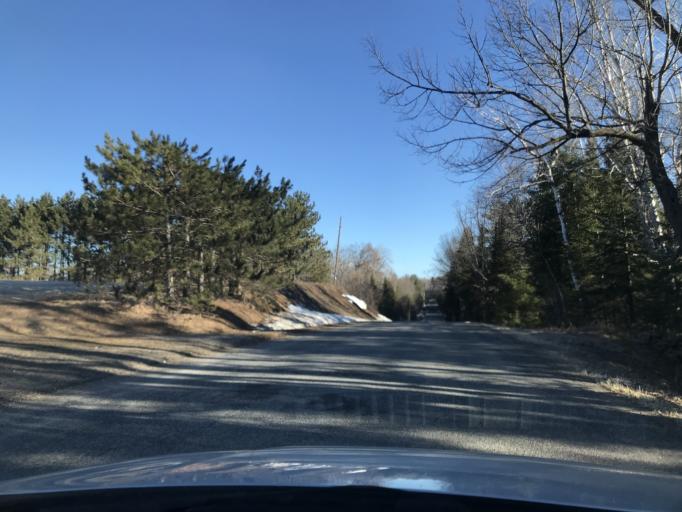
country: US
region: Wisconsin
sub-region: Marinette County
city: Niagara
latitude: 45.3618
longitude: -88.0296
